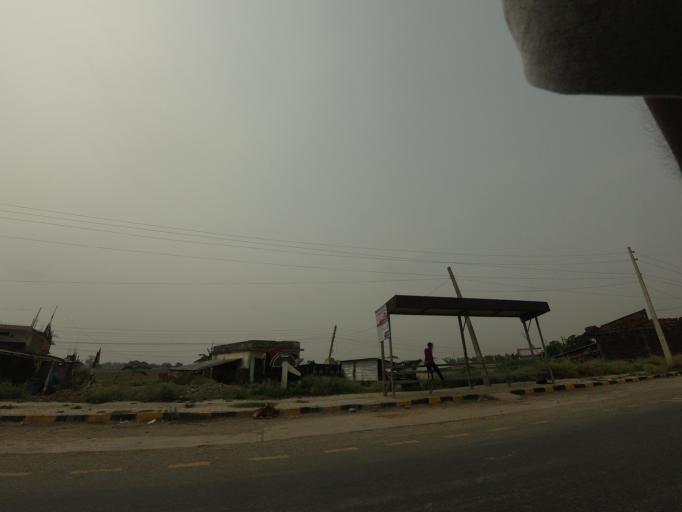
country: IN
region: Uttar Pradesh
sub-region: Maharajganj
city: Nautanwa
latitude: 27.5023
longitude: 83.3422
